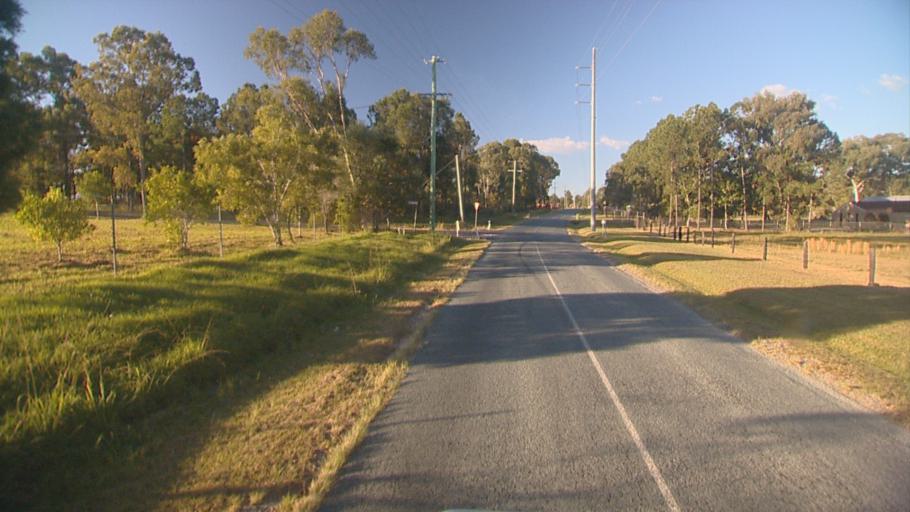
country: AU
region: Queensland
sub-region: Logan
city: Logan Reserve
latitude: -27.7278
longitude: 153.0973
